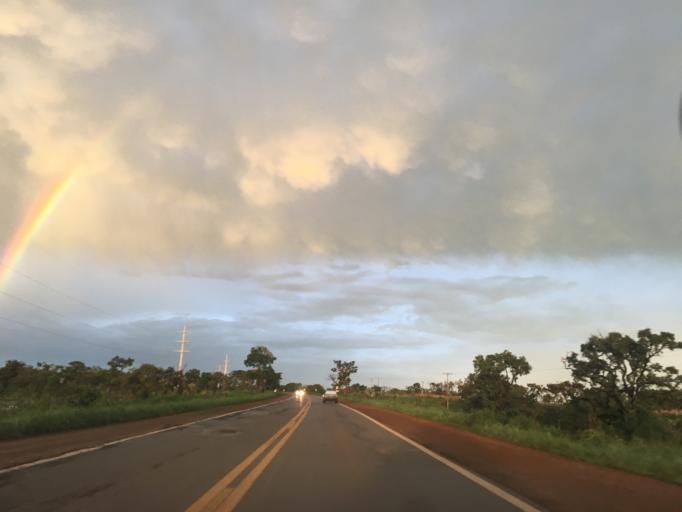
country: BR
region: Federal District
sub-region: Brasilia
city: Brasilia
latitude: -15.9752
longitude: -47.9679
